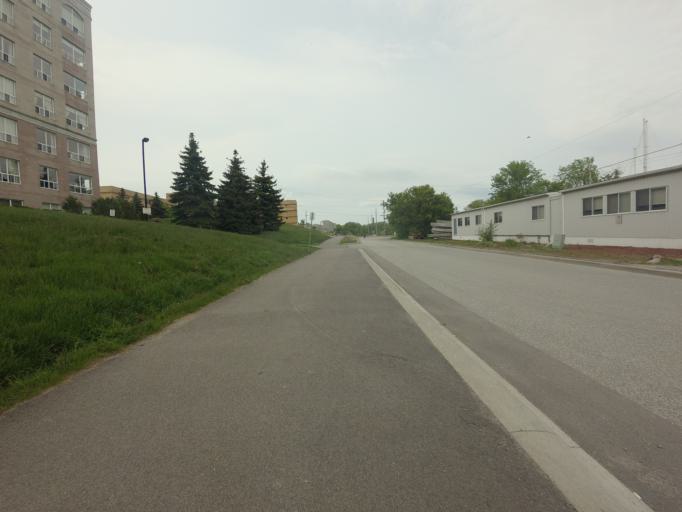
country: CA
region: Ontario
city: Kingston
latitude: 44.2367
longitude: -76.4812
